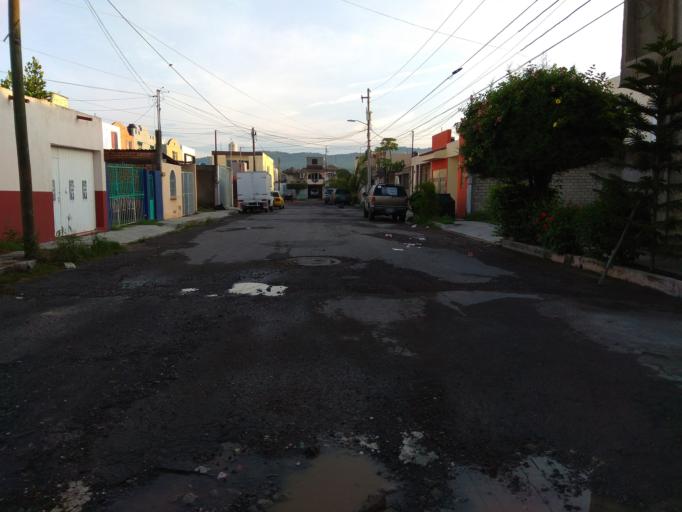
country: MX
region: Nayarit
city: Tepic
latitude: 21.4836
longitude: -104.8549
